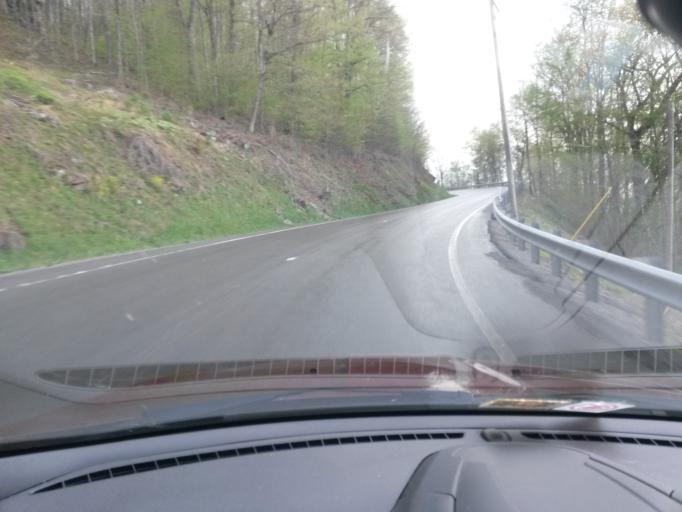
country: US
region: Virginia
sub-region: Highland County
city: Monterey
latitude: 38.5940
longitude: -79.8477
